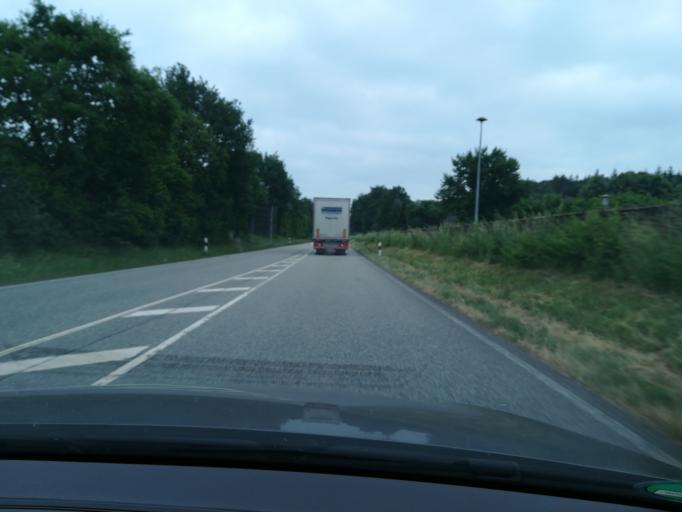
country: DE
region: Schleswig-Holstein
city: Kasseburg
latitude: 53.5542
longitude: 10.4137
